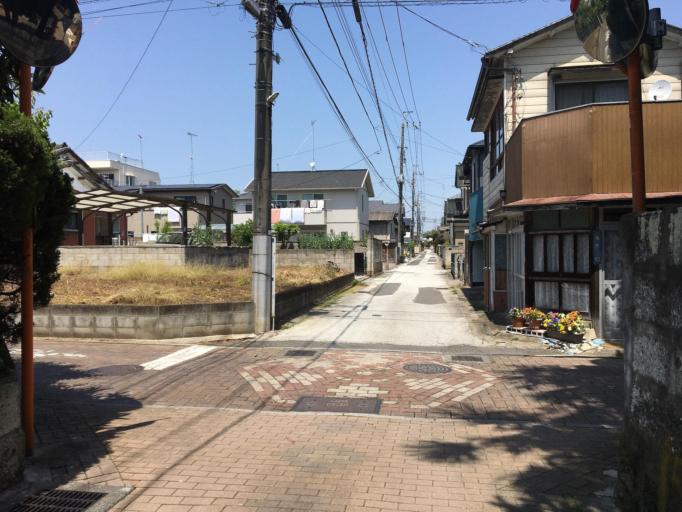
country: JP
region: Ibaraki
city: Koga
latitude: 36.1979
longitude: 139.6984
